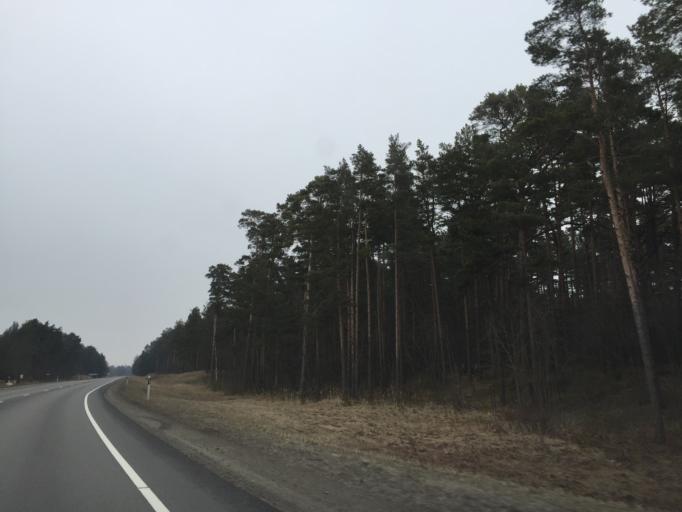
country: EE
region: Paernumaa
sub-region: Paernu linn
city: Parnu
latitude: 58.2006
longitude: 24.4859
